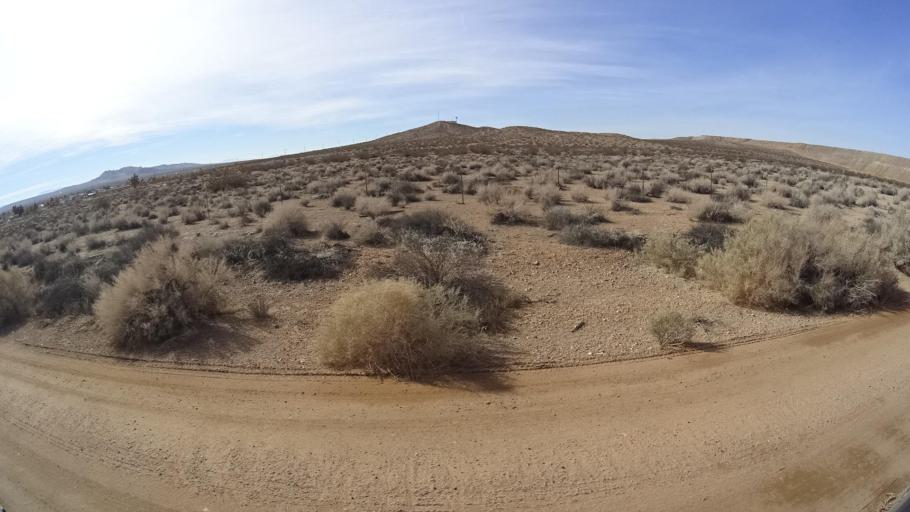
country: US
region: California
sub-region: Kern County
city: Boron
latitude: 35.0188
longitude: -117.6514
